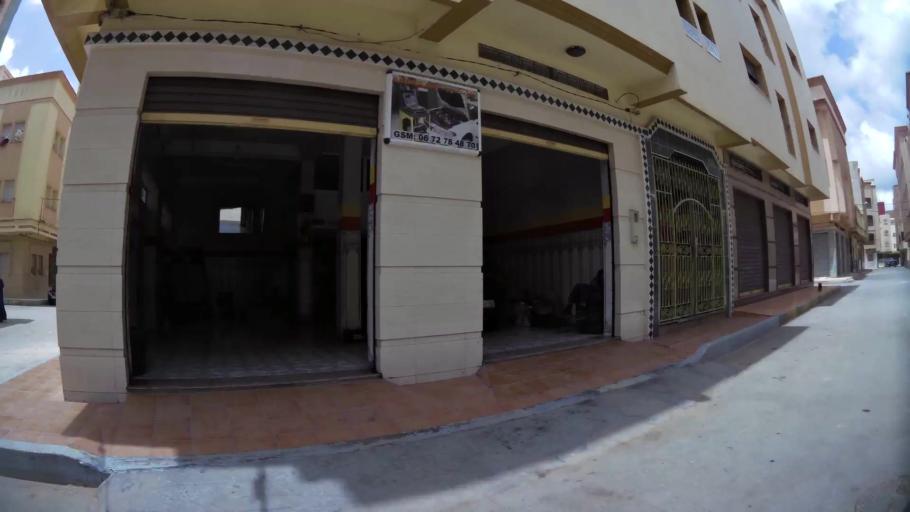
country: MA
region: Oriental
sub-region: Nador
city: Nador
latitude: 35.1677
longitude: -2.9197
